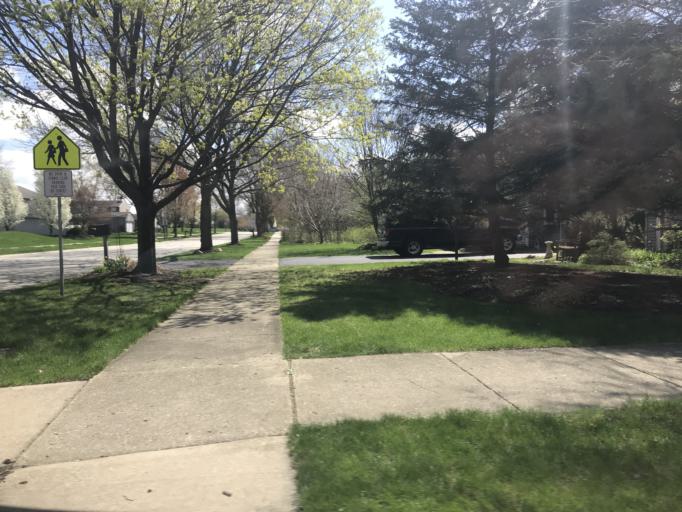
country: US
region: Illinois
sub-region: Will County
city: Bolingbrook
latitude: 41.7374
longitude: -88.1131
